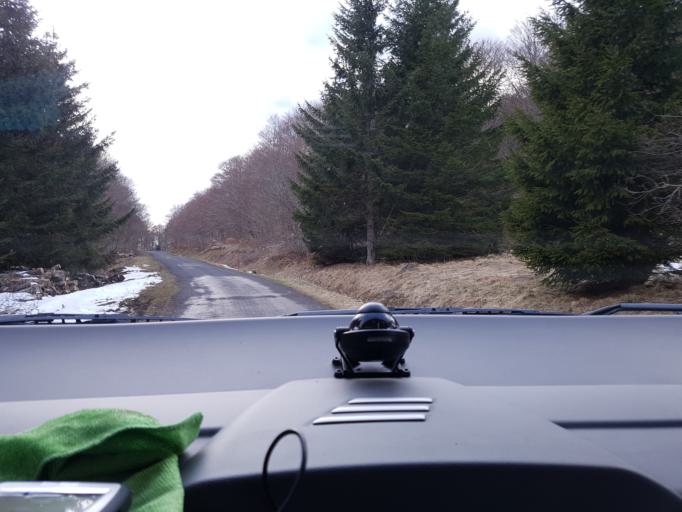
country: FR
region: Midi-Pyrenees
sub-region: Departement de l'Aveyron
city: Laguiole
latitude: 44.6518
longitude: 2.9346
